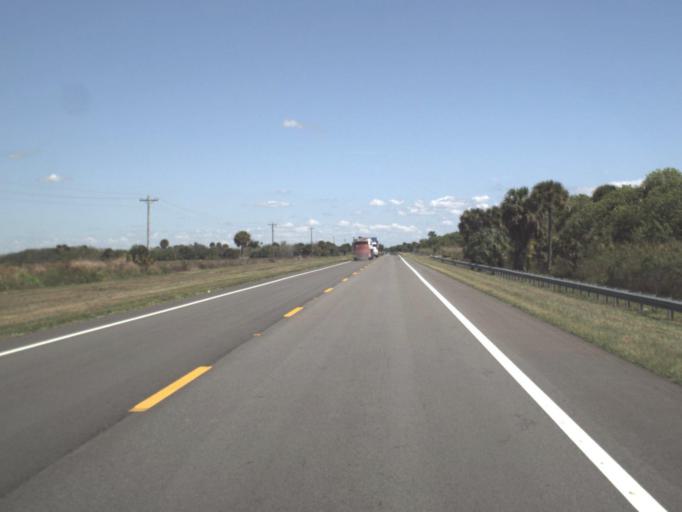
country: US
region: Florida
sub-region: Glades County
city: Buckhead Ridge
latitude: 27.0309
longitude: -81.0065
